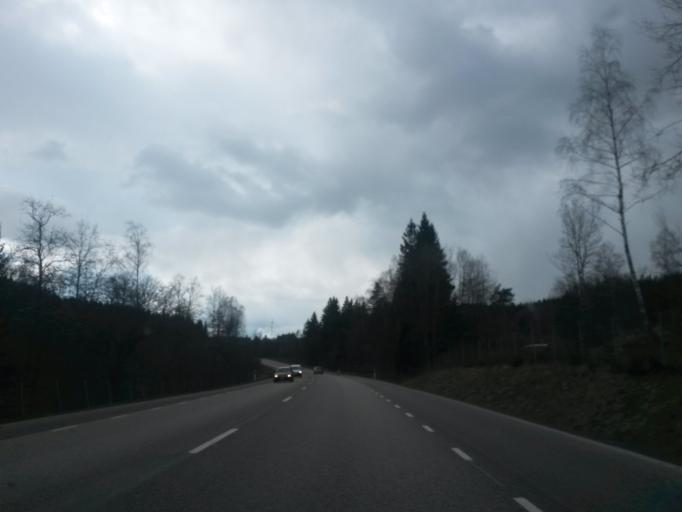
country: SE
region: Vaestra Goetaland
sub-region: Skovde Kommun
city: Skoevde
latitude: 58.3931
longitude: 13.7773
